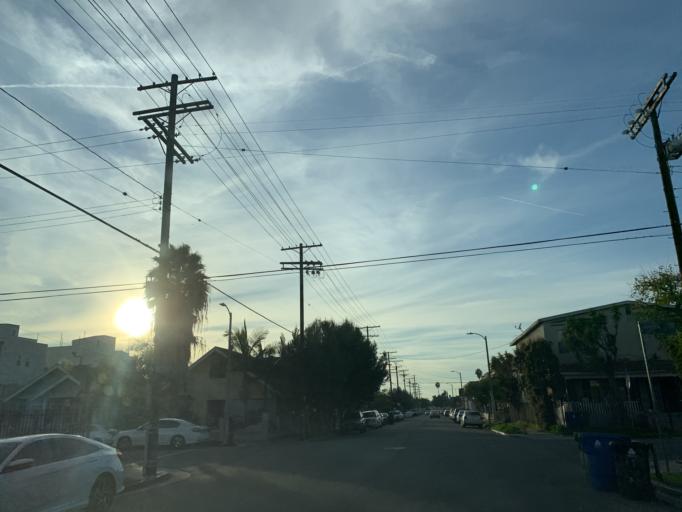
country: US
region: California
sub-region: Los Angeles County
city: Silver Lake
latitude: 34.0491
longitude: -118.2976
